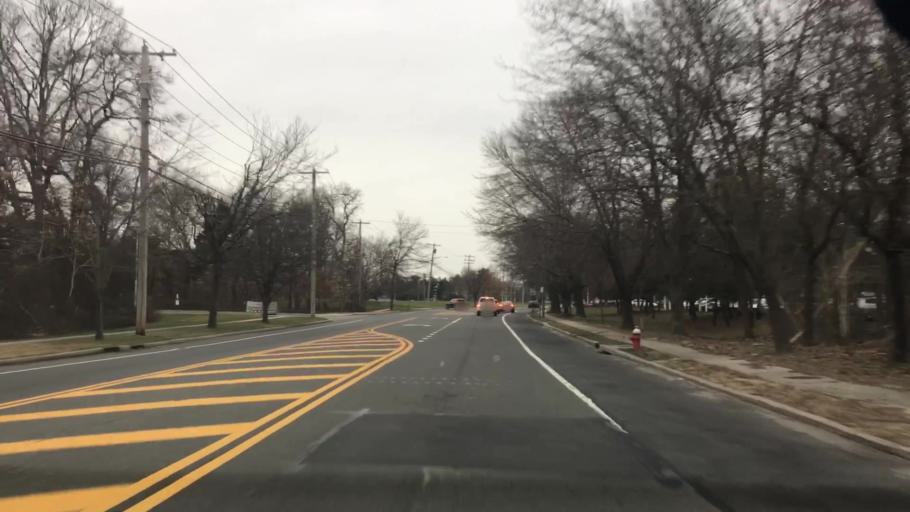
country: US
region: New York
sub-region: Suffolk County
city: Melville
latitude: 40.7829
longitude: -73.4232
